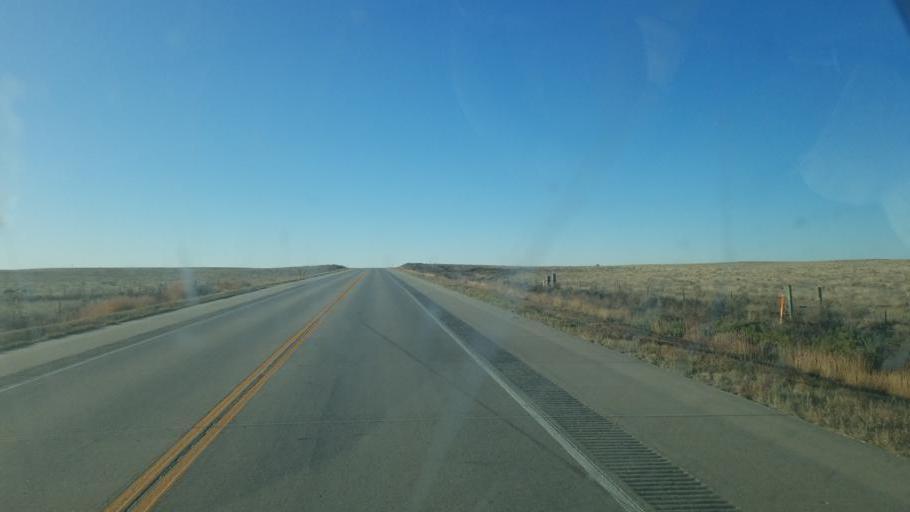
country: US
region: Colorado
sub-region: Kiowa County
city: Eads
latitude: 38.5424
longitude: -102.7859
